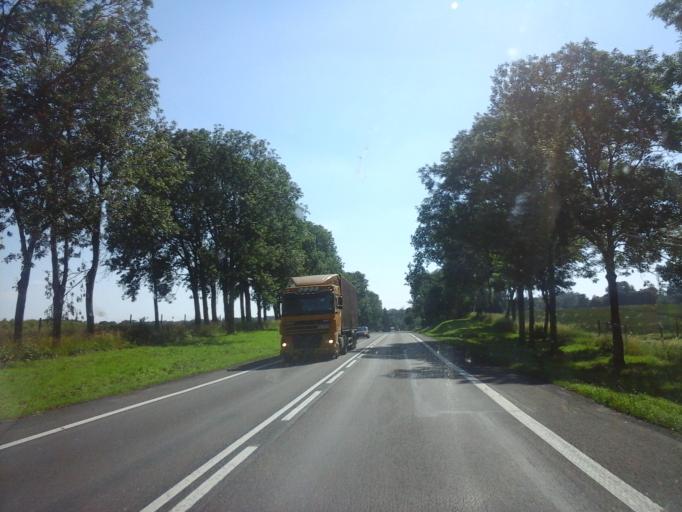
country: PL
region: West Pomeranian Voivodeship
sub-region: Powiat bialogardzki
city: Karlino
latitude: 54.0182
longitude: 15.8307
